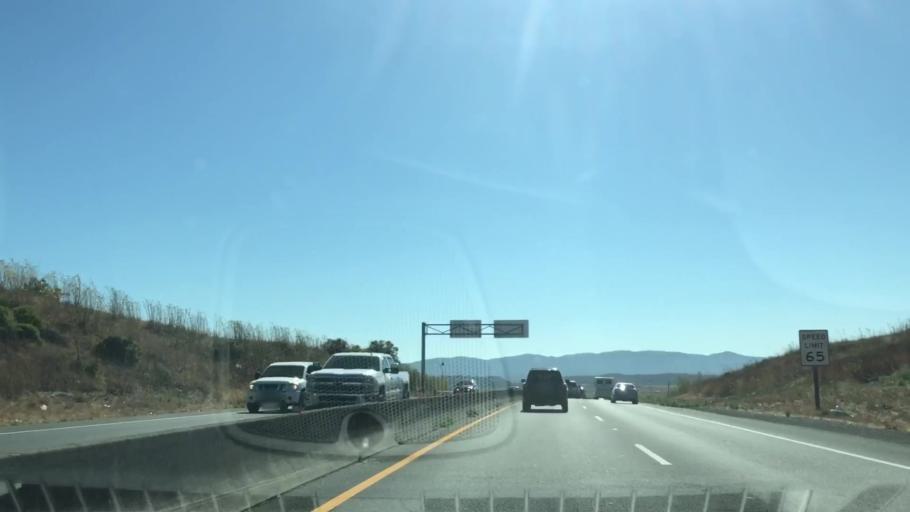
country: US
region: California
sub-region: Marin County
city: Black Point-Green Point
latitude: 38.1466
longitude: -122.4558
